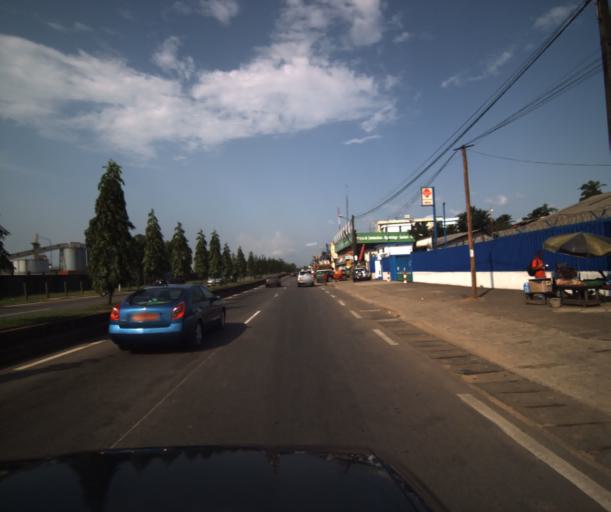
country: CM
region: Littoral
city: Douala
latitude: 4.0534
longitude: 9.6926
